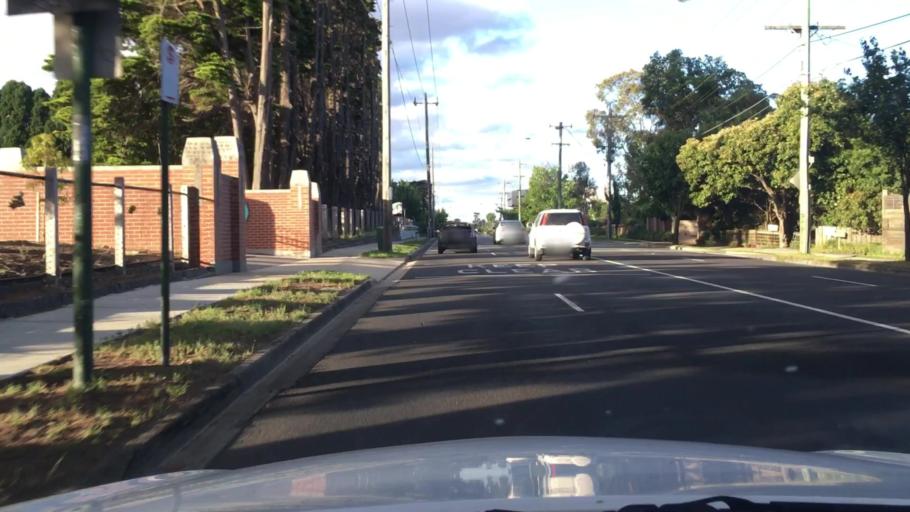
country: AU
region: Victoria
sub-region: Whitehorse
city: Box Hill
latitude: -37.8226
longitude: 145.1378
